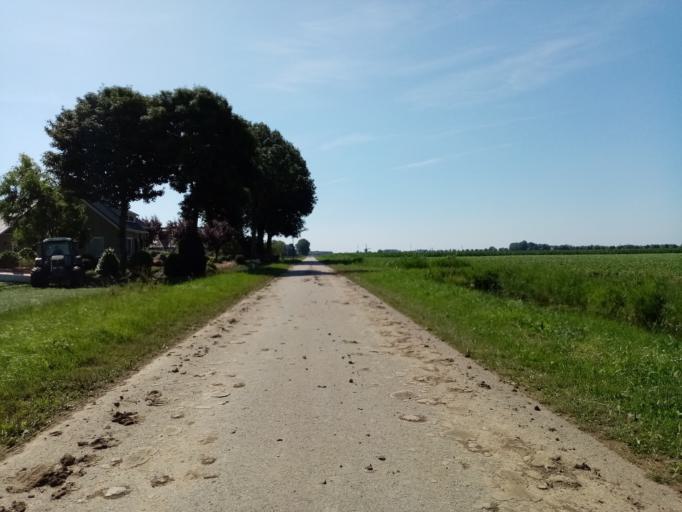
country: NL
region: North Brabant
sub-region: Gemeente Moerdijk
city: Klundert
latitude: 51.6217
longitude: 4.6490
